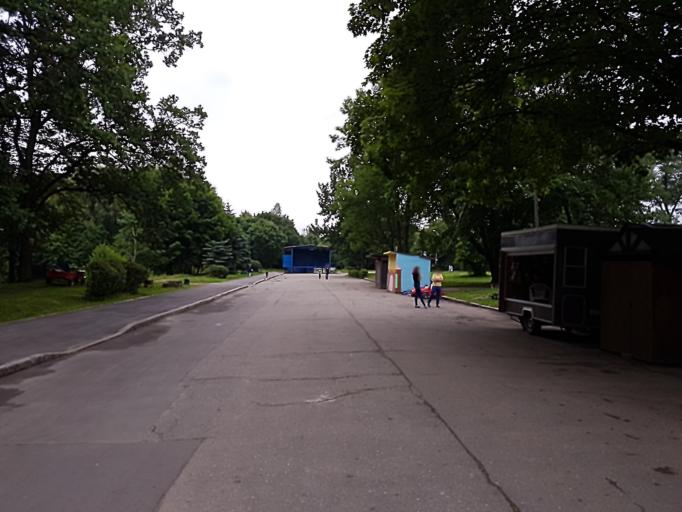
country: RU
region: Kaliningrad
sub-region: Gorod Kaliningrad
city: Kaliningrad
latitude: 54.6928
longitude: 20.5147
